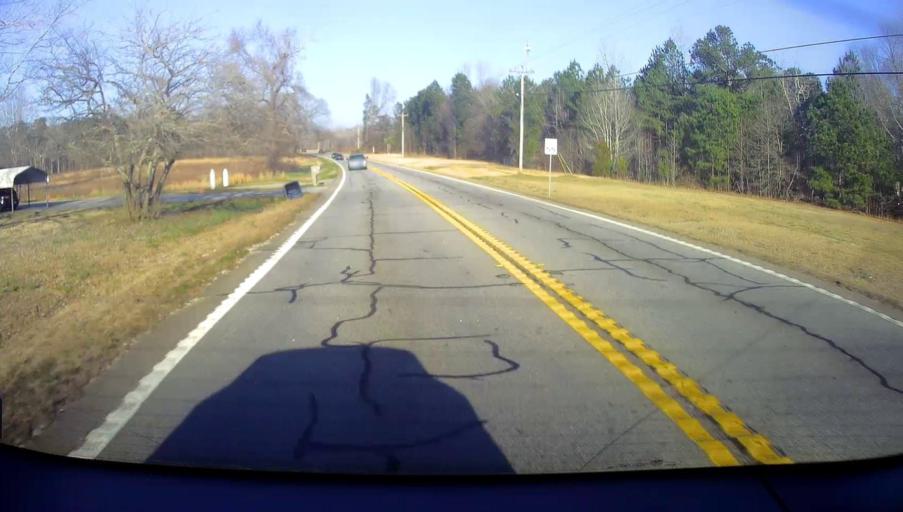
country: US
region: Georgia
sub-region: Henry County
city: Hampton
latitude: 33.4205
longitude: -84.2278
